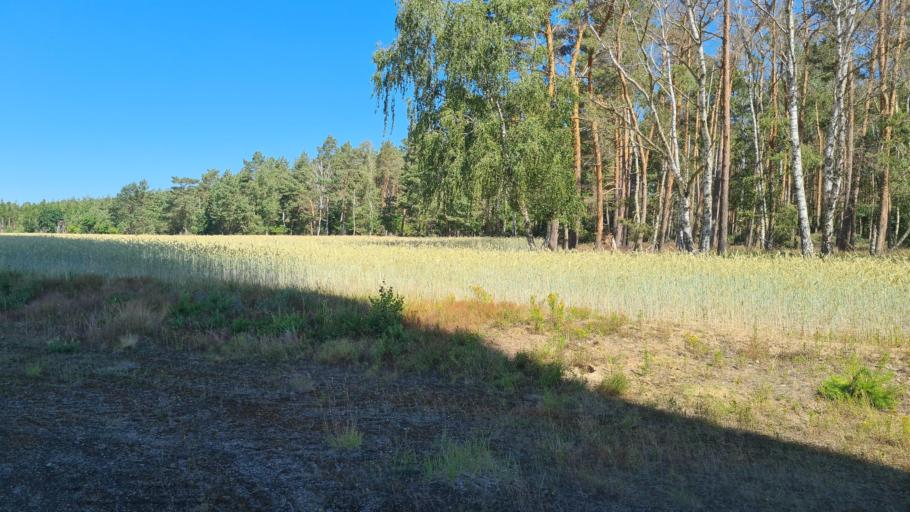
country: DE
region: Brandenburg
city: Treuenbrietzen
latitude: 52.0234
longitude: 12.8744
